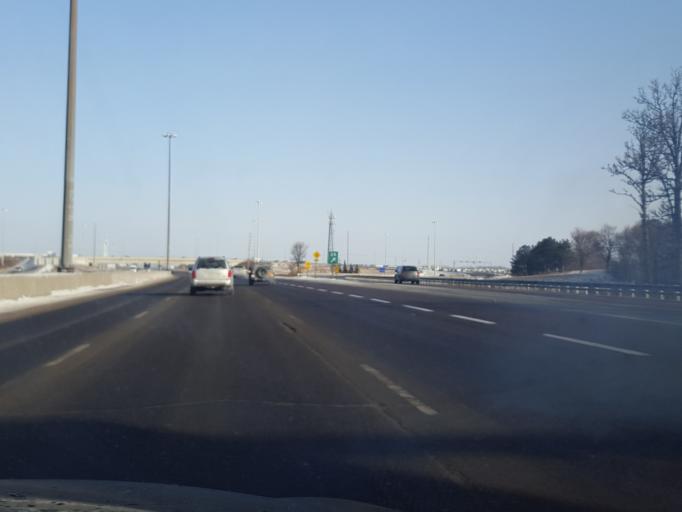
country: CA
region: Ontario
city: Vaughan
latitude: 43.8418
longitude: -79.5475
